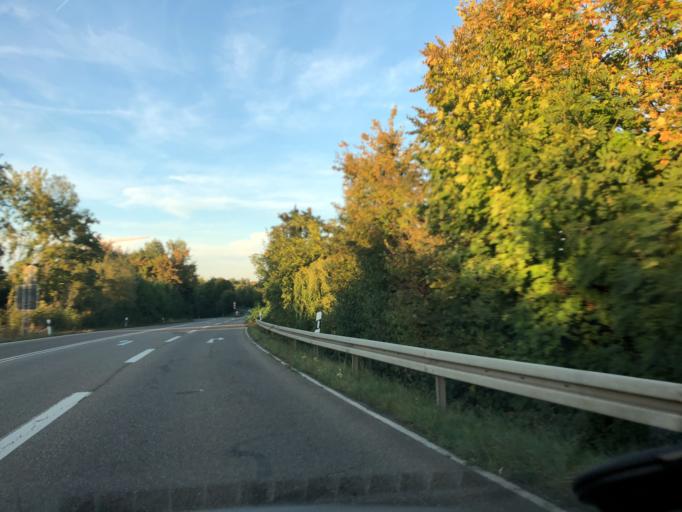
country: DE
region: Baden-Wuerttemberg
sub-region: Regierungsbezirk Stuttgart
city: Kornwestheim
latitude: 48.8471
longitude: 9.1821
